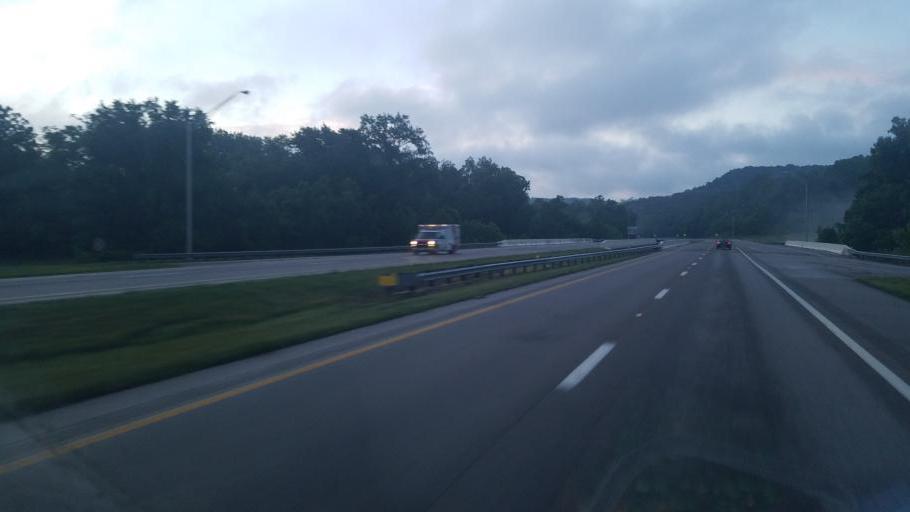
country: US
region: Ohio
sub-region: Pike County
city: Waverly
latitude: 39.1985
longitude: -82.8153
